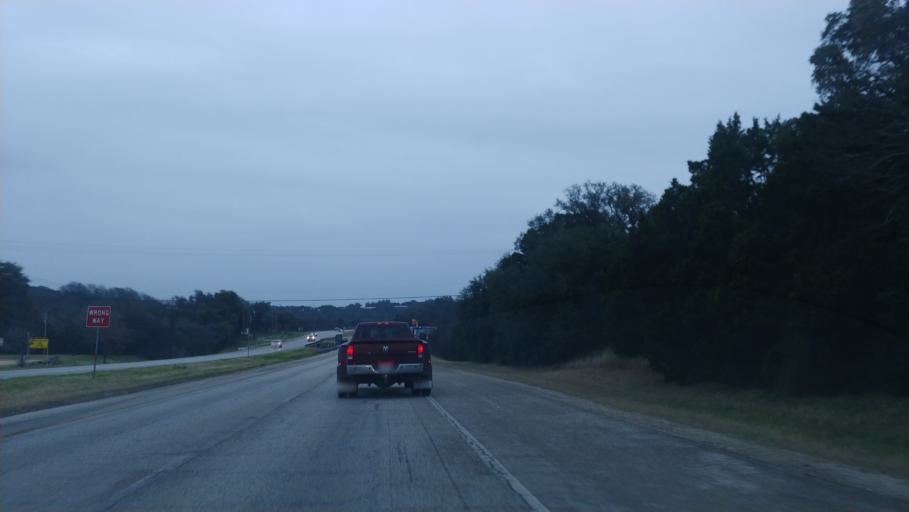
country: US
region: Texas
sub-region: Bexar County
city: Helotes
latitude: 29.5809
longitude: -98.6920
